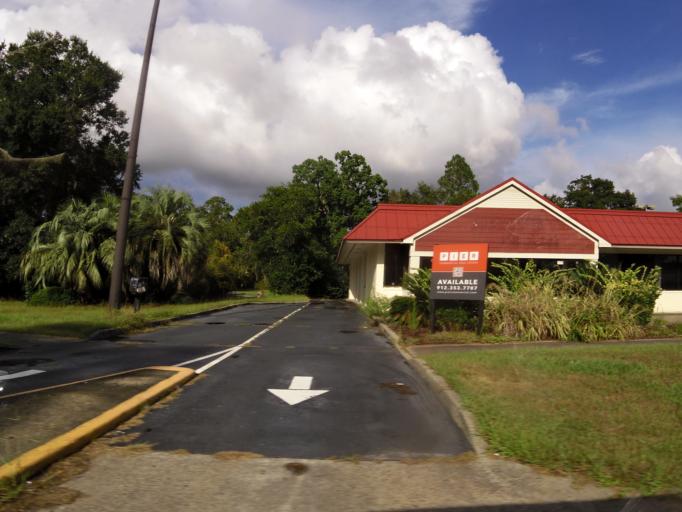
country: US
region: Georgia
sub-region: Liberty County
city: Hinesville
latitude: 31.8456
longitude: -81.6025
